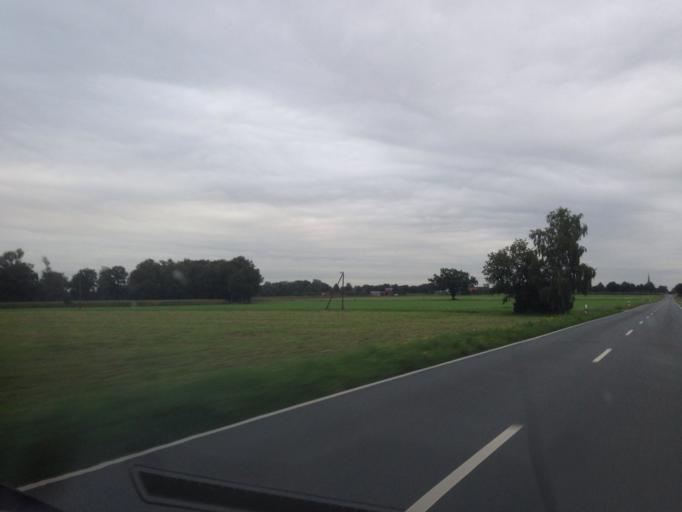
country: DE
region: North Rhine-Westphalia
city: Olfen
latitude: 51.7462
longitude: 7.4022
